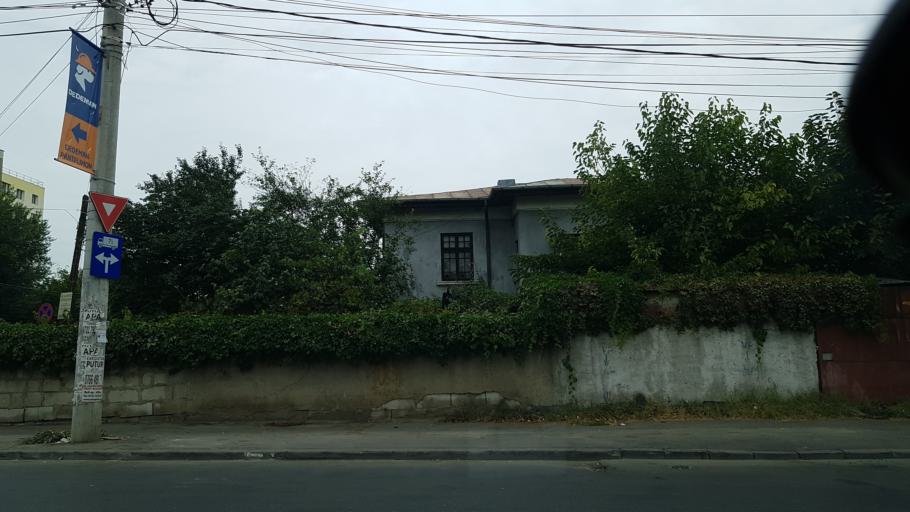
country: RO
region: Ilfov
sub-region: Comuna Fundeni-Dobroesti
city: Fundeni
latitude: 44.4438
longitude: 26.1661
